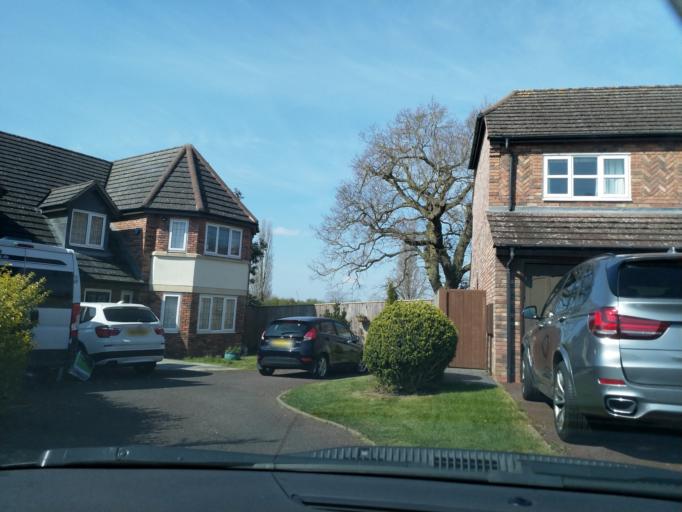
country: GB
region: England
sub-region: Warwickshire
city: Stratford-upon-Avon
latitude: 52.1937
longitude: -1.7265
